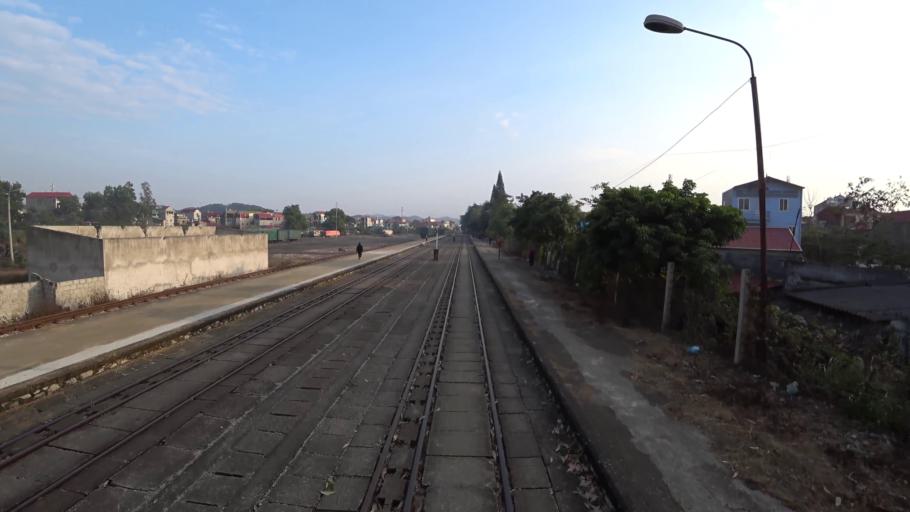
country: VN
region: Lang Son
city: Thi Tran Cao Loc
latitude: 21.8665
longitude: 106.7633
